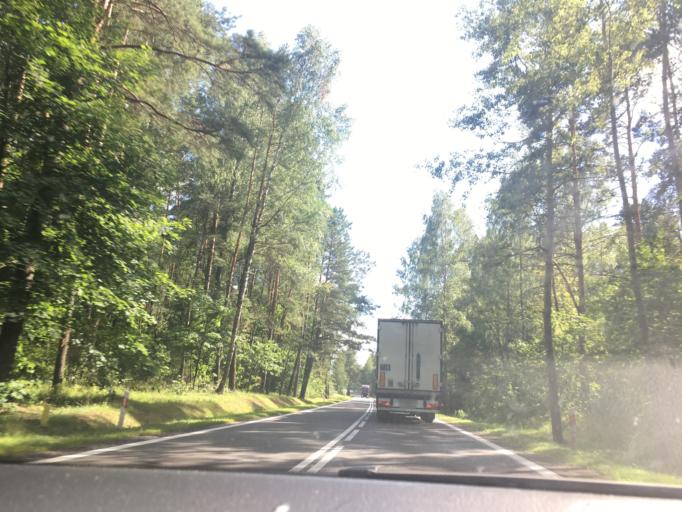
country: PL
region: Podlasie
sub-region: Powiat sokolski
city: Suchowola
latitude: 53.6502
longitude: 23.1200
